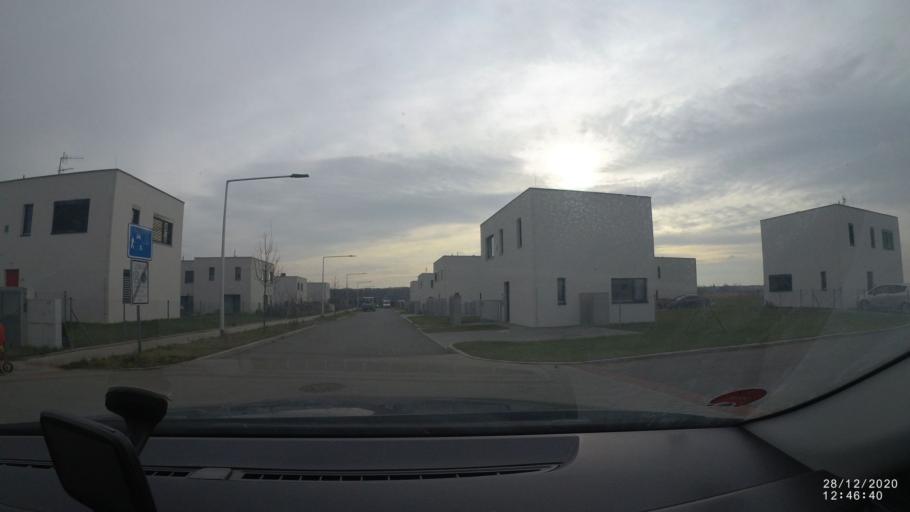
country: CZ
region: Praha
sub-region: Praha 19
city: Kbely
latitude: 50.1572
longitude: 14.5705
